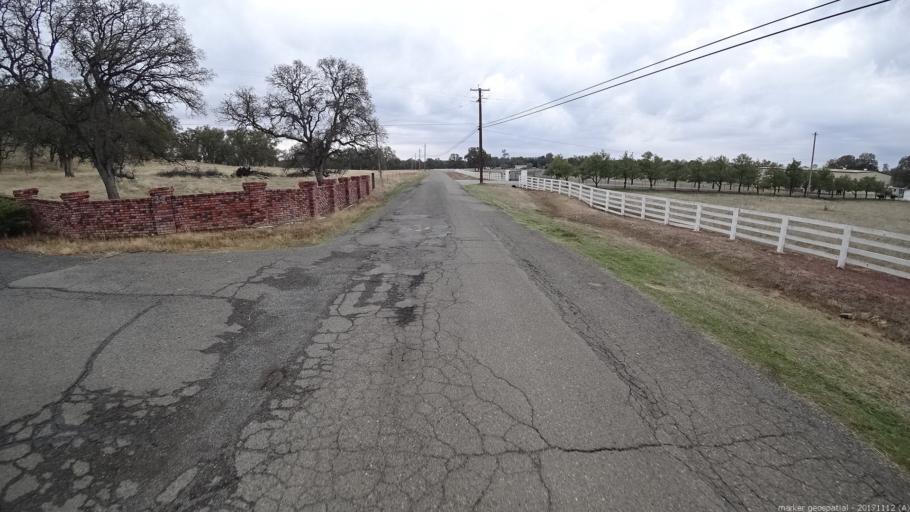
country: US
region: California
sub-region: Shasta County
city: Palo Cedro
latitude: 40.5324
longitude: -122.2264
